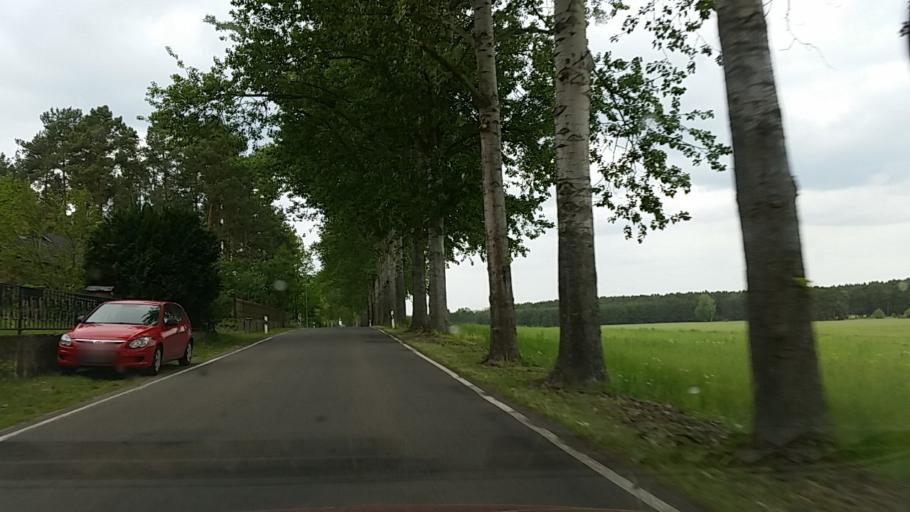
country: DE
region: Brandenburg
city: Rauen
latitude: 52.3167
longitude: 13.9630
